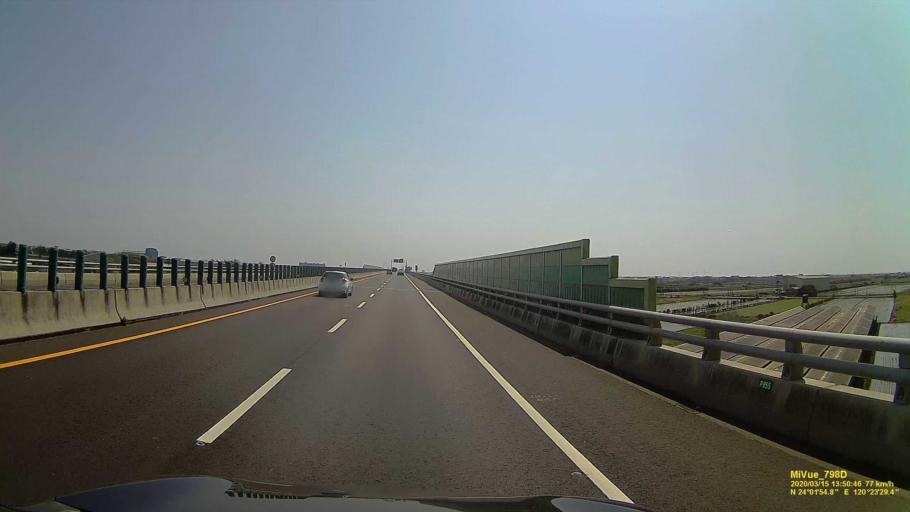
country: TW
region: Taiwan
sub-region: Changhua
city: Chang-hua
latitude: 24.0318
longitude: 120.3911
